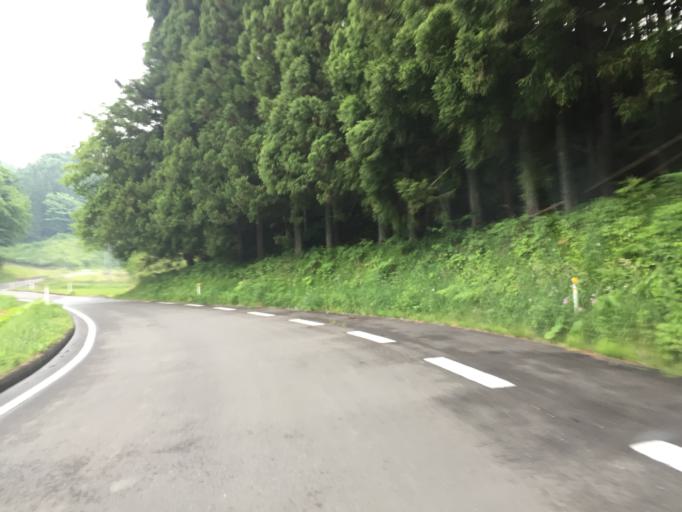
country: JP
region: Fukushima
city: Ishikawa
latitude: 37.1465
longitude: 140.5355
